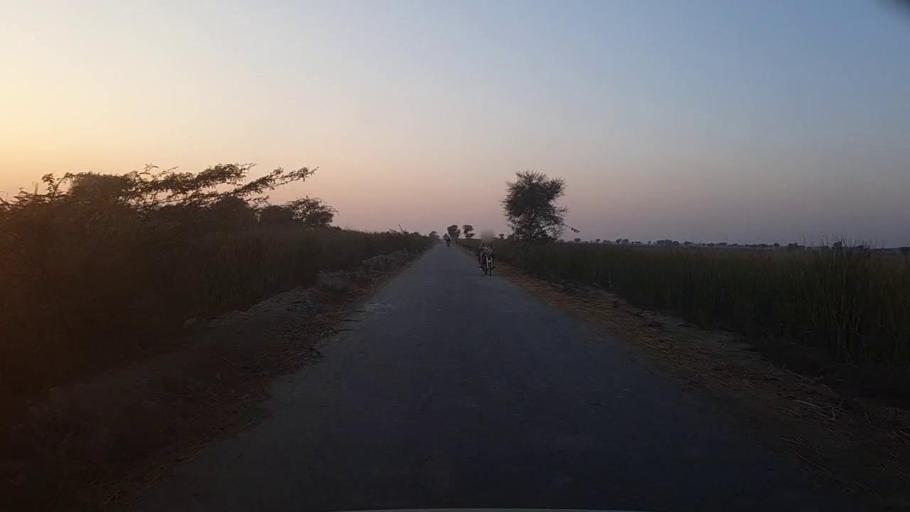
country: PK
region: Sindh
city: Khairpur Nathan Shah
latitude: 27.1589
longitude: 67.7112
